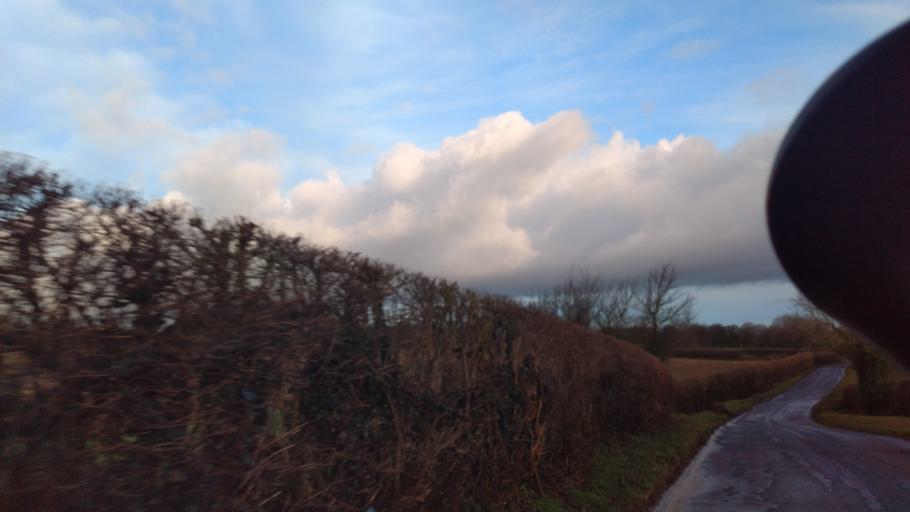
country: GB
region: England
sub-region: Wiltshire
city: Corsham
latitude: 51.4602
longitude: -2.1622
